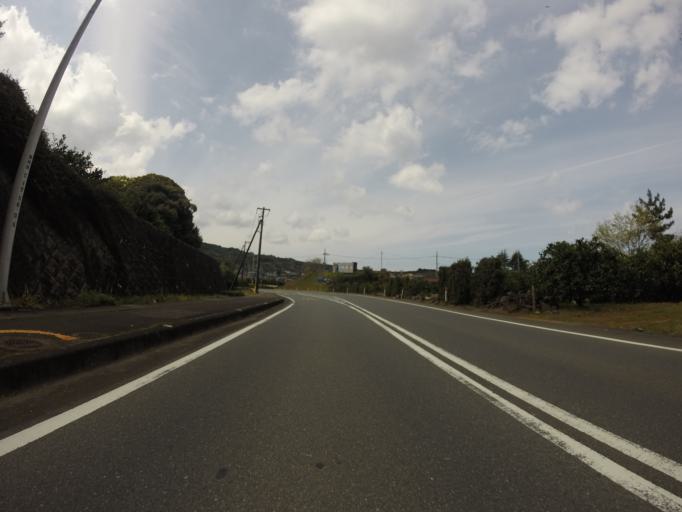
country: JP
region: Shizuoka
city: Numazu
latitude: 35.0195
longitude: 138.8821
